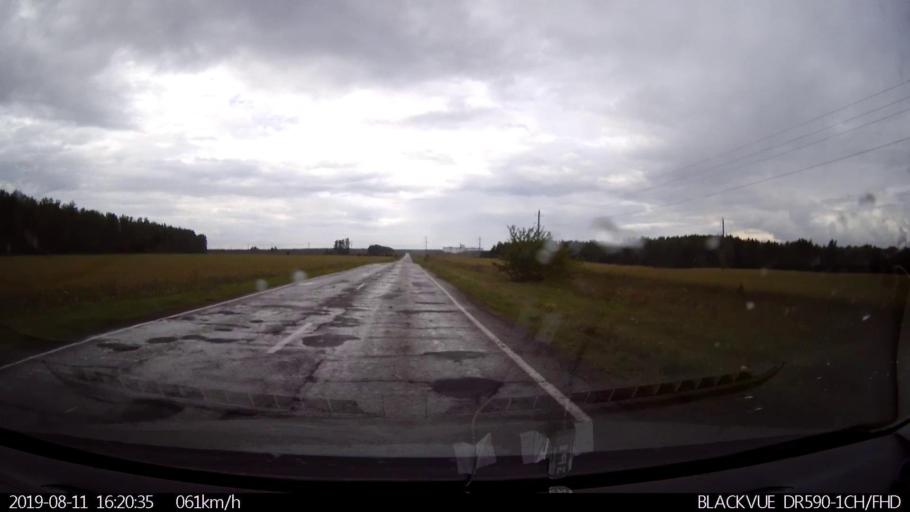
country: RU
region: Ulyanovsk
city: Mayna
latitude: 54.0729
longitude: 47.6022
